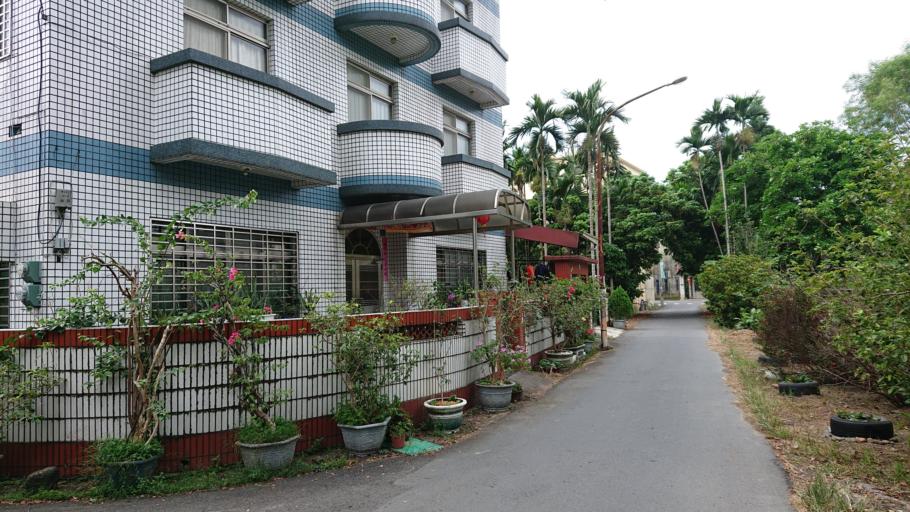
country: TW
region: Taiwan
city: Lugu
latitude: 23.7503
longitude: 120.6776
